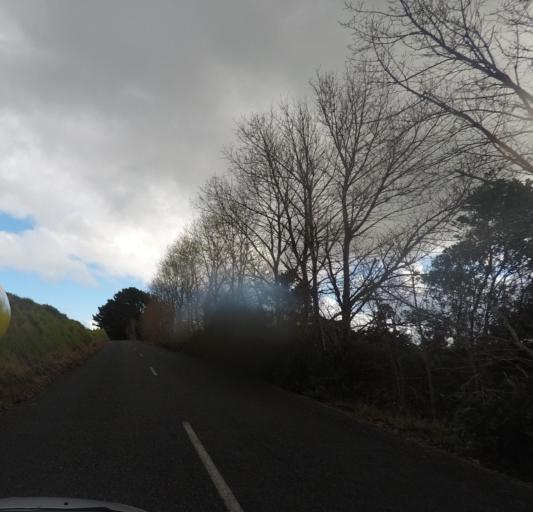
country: NZ
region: Auckland
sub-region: Auckland
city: Warkworth
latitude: -36.3731
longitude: 174.7632
